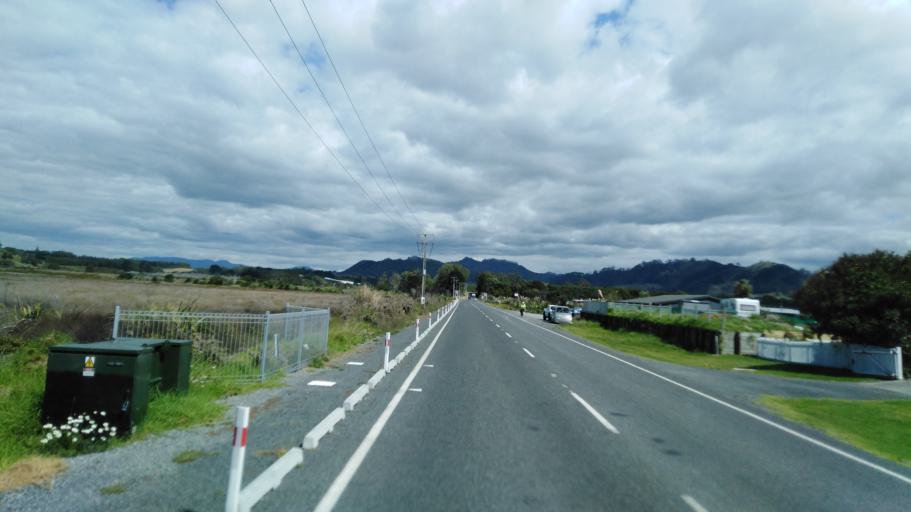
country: NZ
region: Bay of Plenty
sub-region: Western Bay of Plenty District
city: Waihi Beach
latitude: -37.4319
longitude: 175.9558
